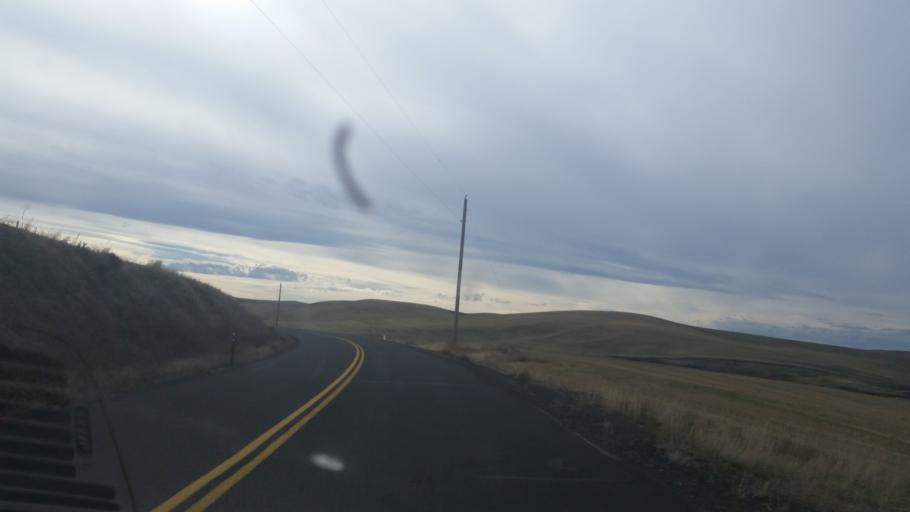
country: US
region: Washington
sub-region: Spokane County
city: Cheney
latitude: 47.3086
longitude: -117.4935
